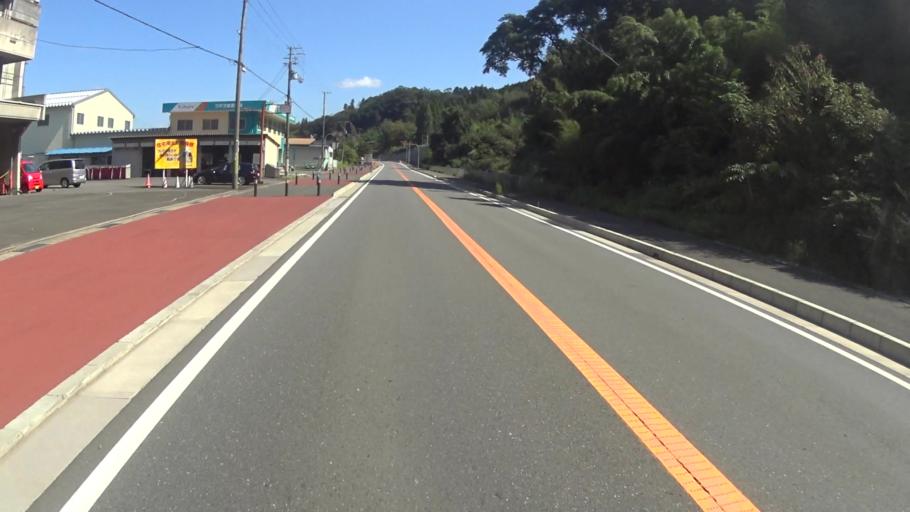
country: JP
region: Kyoto
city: Ayabe
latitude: 35.3036
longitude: 135.2724
